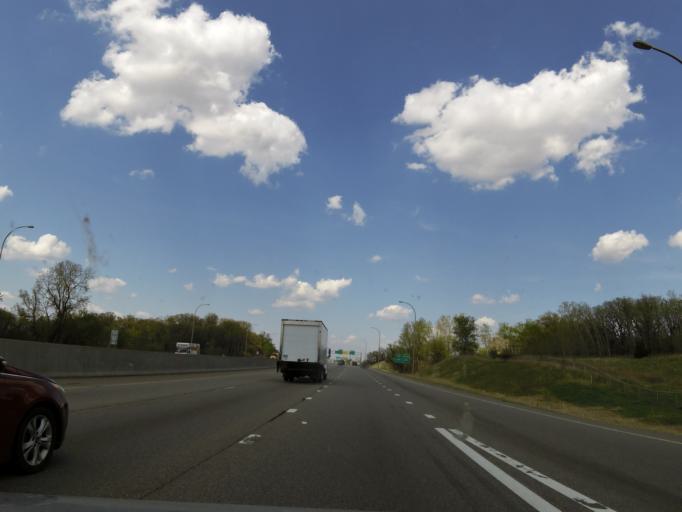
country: US
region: Minnesota
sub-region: Washington County
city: Woodbury
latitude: 44.9416
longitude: -92.9592
